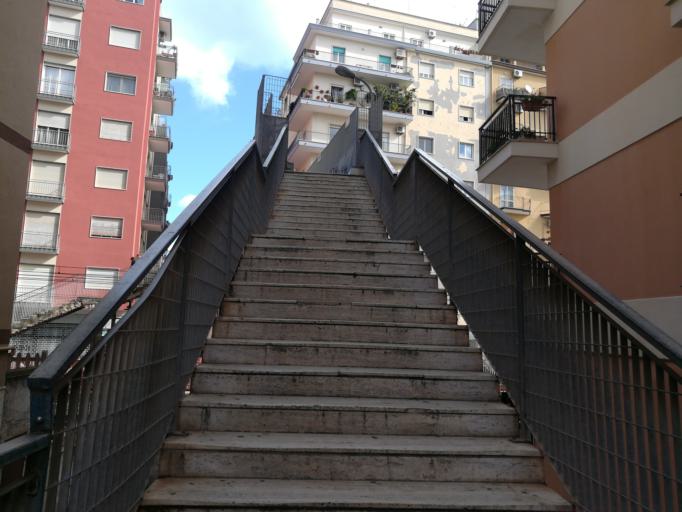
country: IT
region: Apulia
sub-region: Provincia di Bari
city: Bari
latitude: 41.1161
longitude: 16.8920
